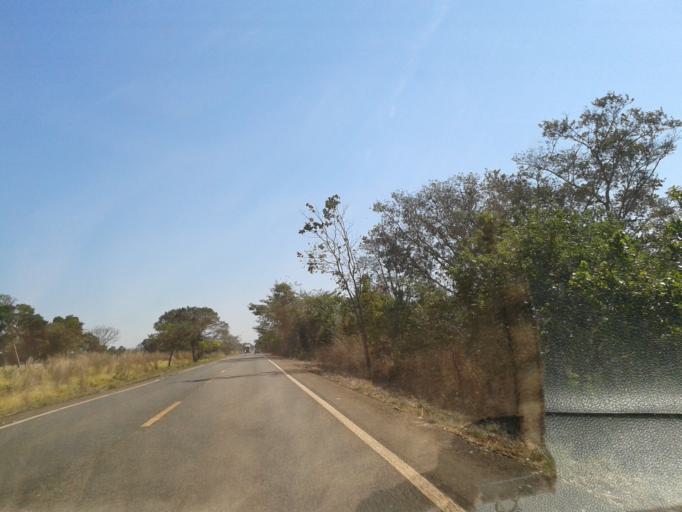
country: BR
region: Goias
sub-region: Sao Miguel Do Araguaia
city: Sao Miguel do Araguaia
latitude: -13.9217
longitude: -50.3225
